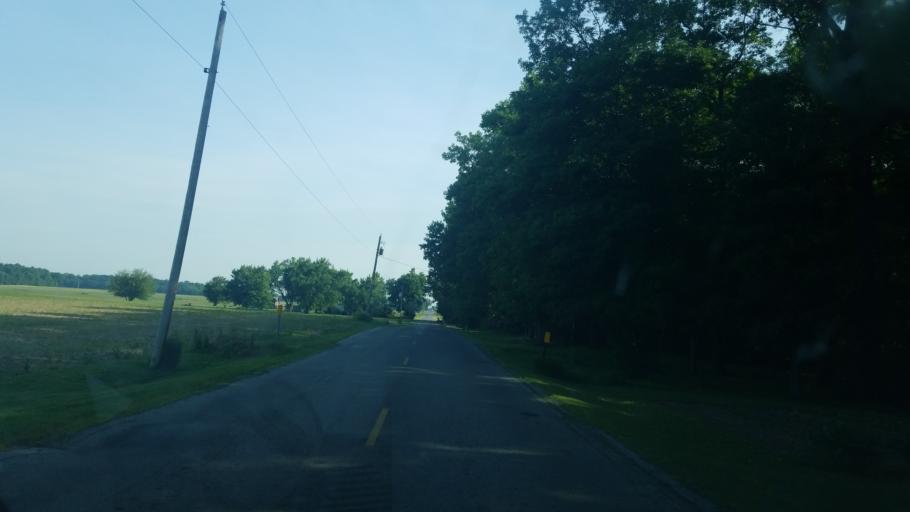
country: US
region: Ohio
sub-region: Hancock County
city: Arlington
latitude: 40.8868
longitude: -83.6986
